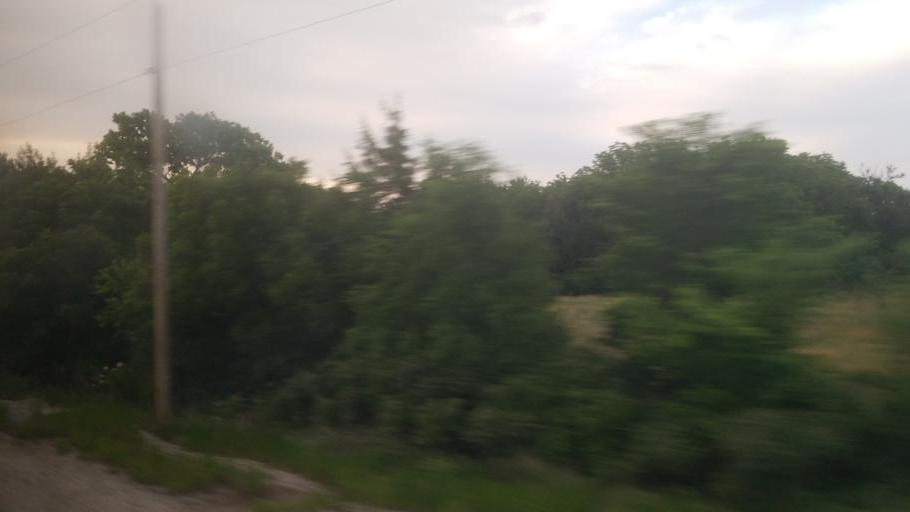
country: US
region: Kansas
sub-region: Marion County
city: Peabody
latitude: 38.1651
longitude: -97.0787
